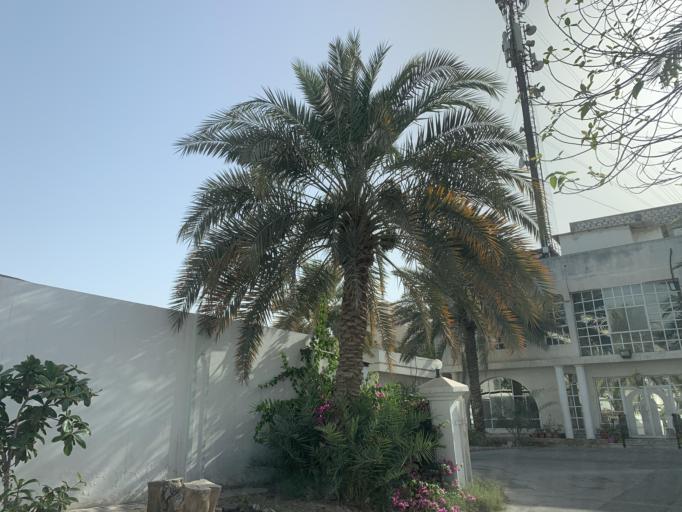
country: BH
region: Northern
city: Ar Rifa'
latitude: 26.1423
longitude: 50.5830
